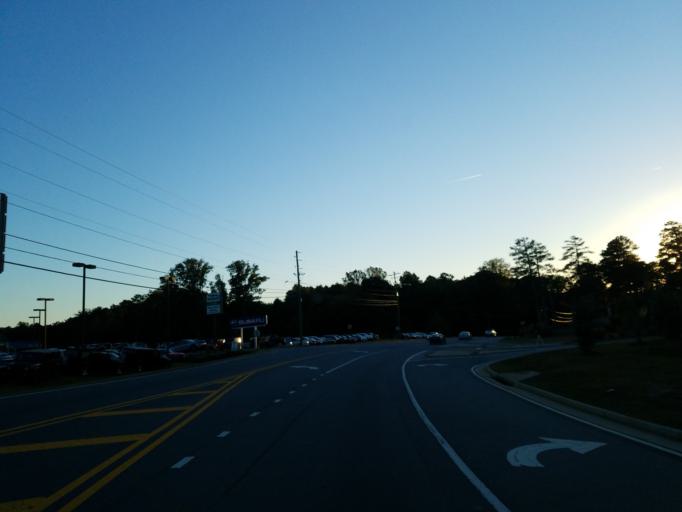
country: US
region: Georgia
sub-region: Forsyth County
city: Cumming
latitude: 34.1815
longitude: -84.1476
